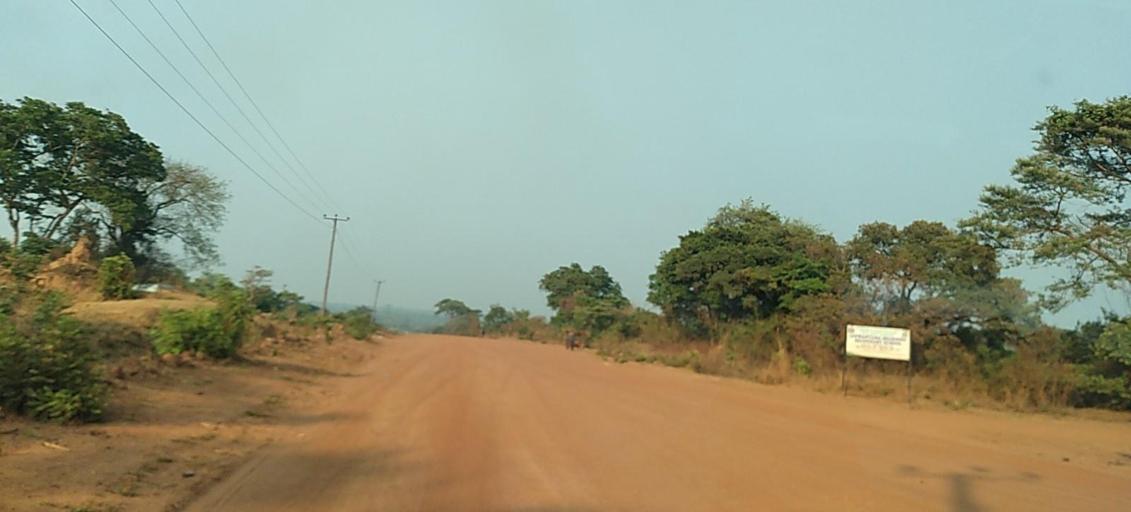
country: ZM
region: Copperbelt
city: Chingola
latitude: -12.8635
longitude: 27.6094
